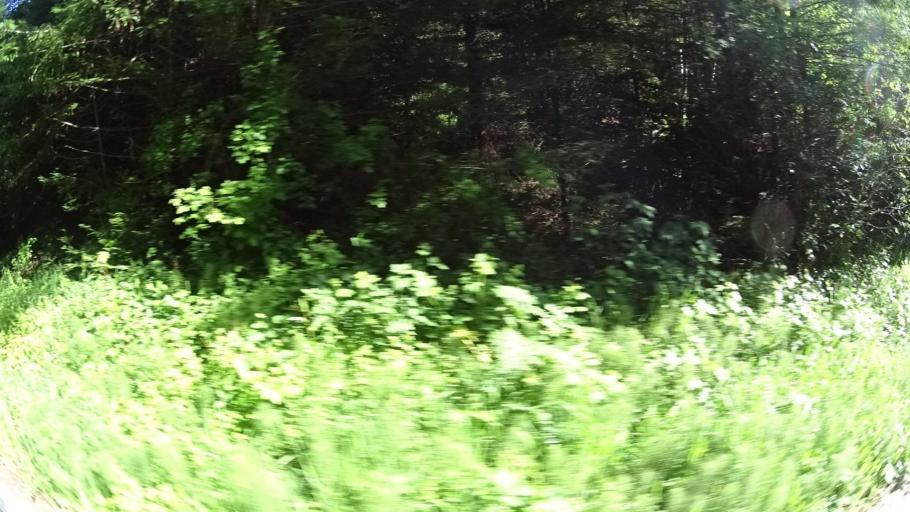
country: US
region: California
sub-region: Humboldt County
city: Rio Dell
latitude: 40.4613
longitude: -124.0486
